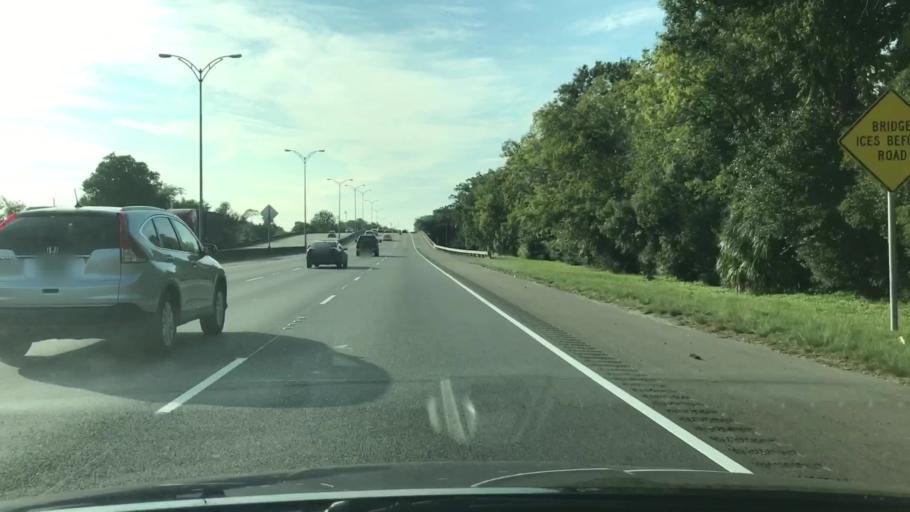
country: US
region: Louisiana
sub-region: Orleans Parish
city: New Orleans
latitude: 29.9934
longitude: -90.0897
